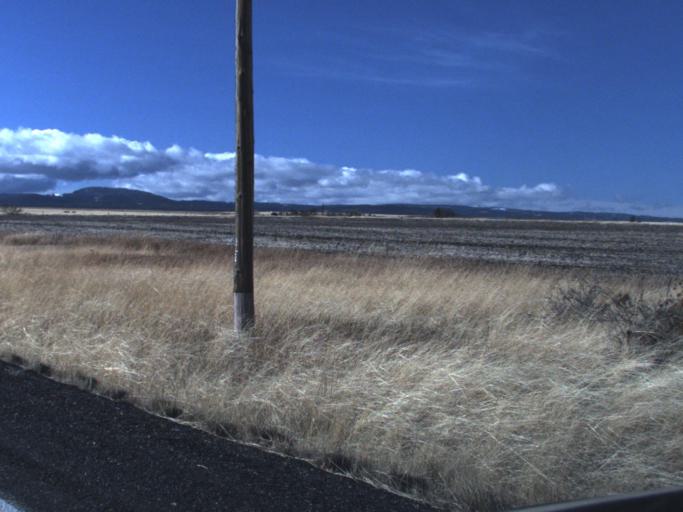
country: US
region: Washington
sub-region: Asotin County
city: Asotin
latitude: 46.1572
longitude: -117.1107
